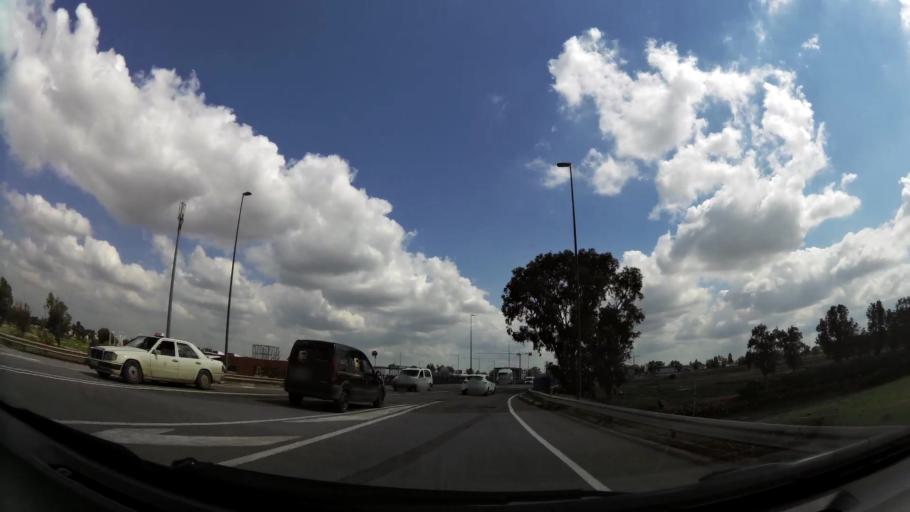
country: MA
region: Chaouia-Ouardigha
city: Nouaseur
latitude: 33.3771
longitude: -7.5686
